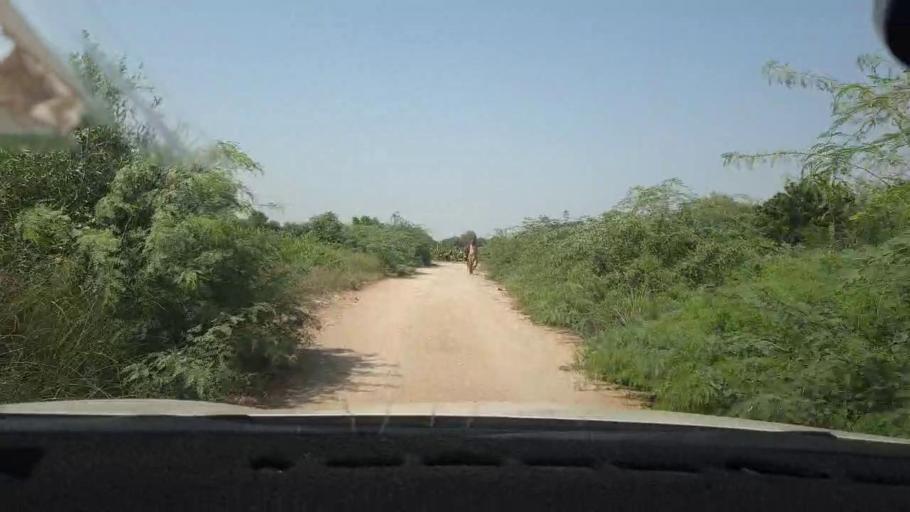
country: PK
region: Sindh
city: Tando Mittha Khan
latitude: 25.8640
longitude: 69.3846
